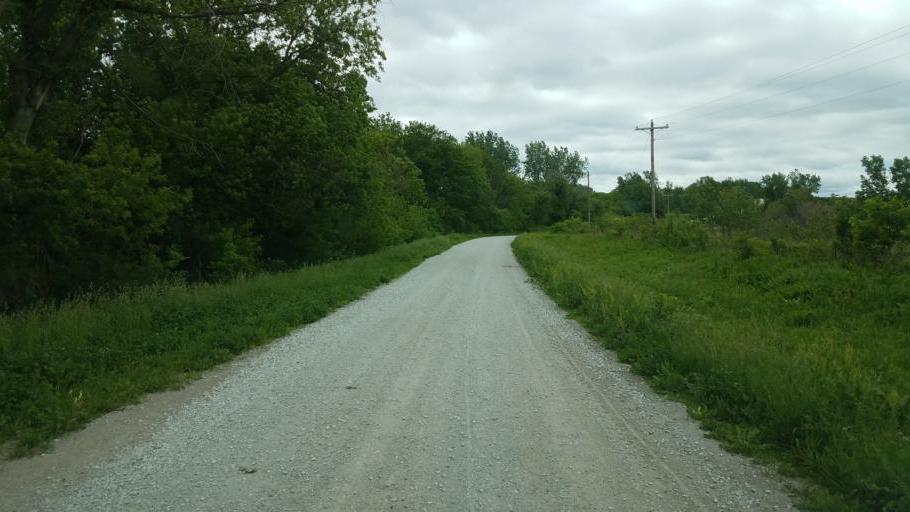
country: US
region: Iowa
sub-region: Decatur County
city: Lamoni
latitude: 40.6381
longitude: -93.8490
